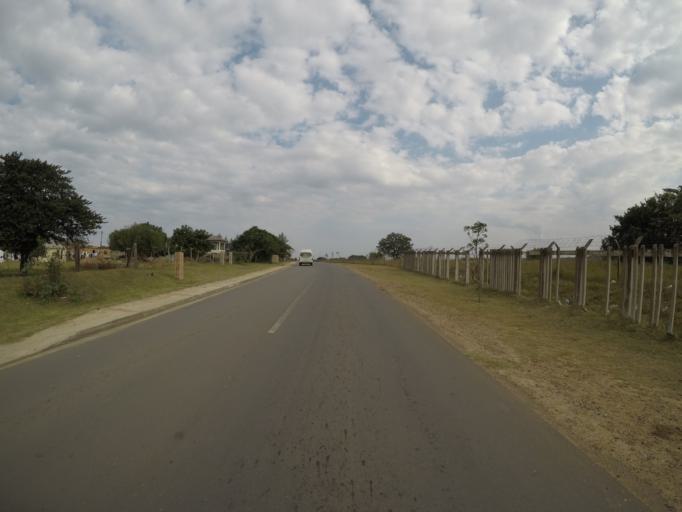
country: ZA
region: KwaZulu-Natal
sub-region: uThungulu District Municipality
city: Richards Bay
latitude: -28.7427
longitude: 32.0922
